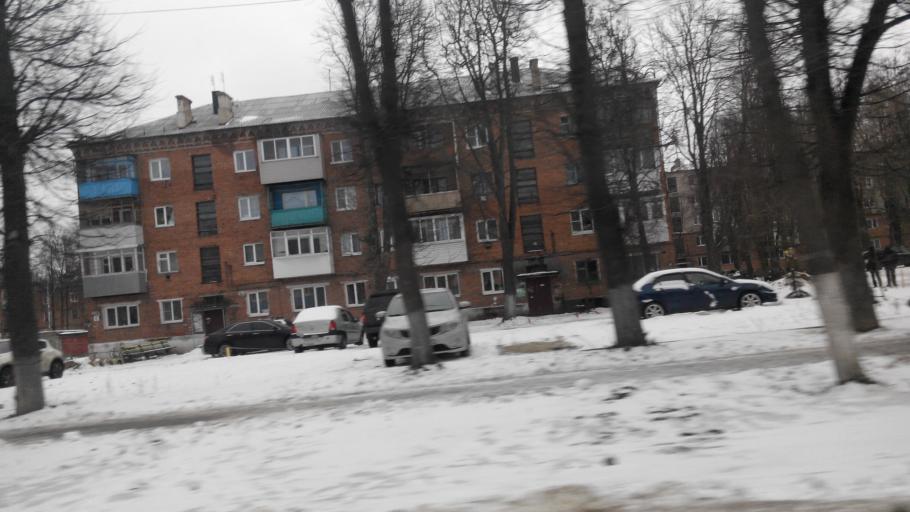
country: RU
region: Tula
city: Uzlovaya
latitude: 53.9655
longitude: 38.1650
